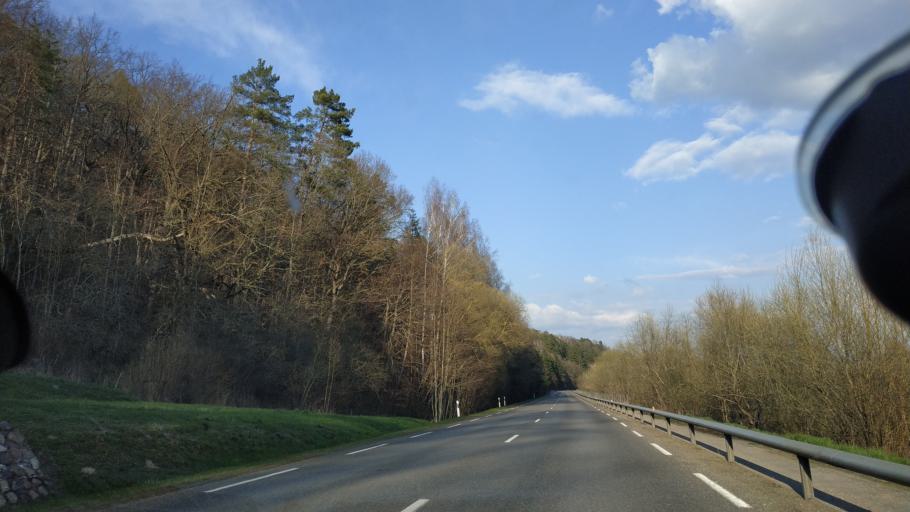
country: LT
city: Vilkija
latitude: 55.0486
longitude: 23.5049
